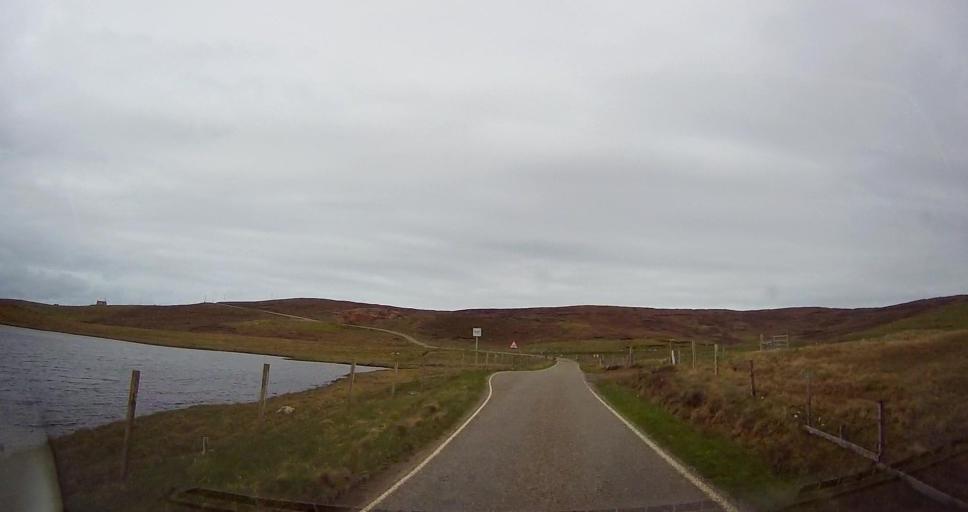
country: GB
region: Scotland
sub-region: Shetland Islands
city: Lerwick
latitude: 60.4860
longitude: -1.5081
